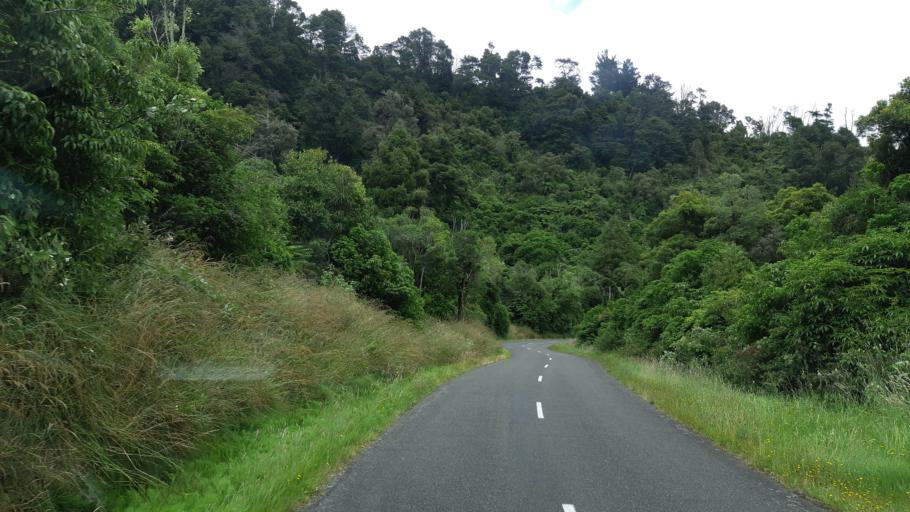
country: NZ
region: Manawatu-Wanganui
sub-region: Palmerston North City
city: Palmerston North
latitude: -39.9398
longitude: 175.9196
